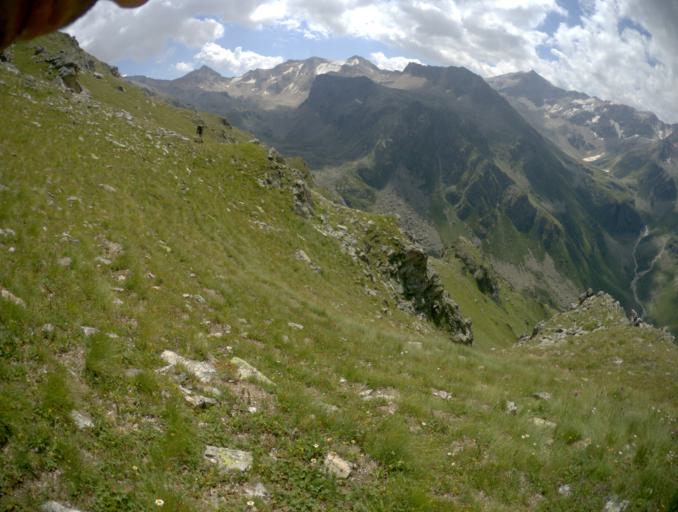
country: RU
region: Karachayevo-Cherkesiya
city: Uchkulan
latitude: 43.2968
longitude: 42.0690
